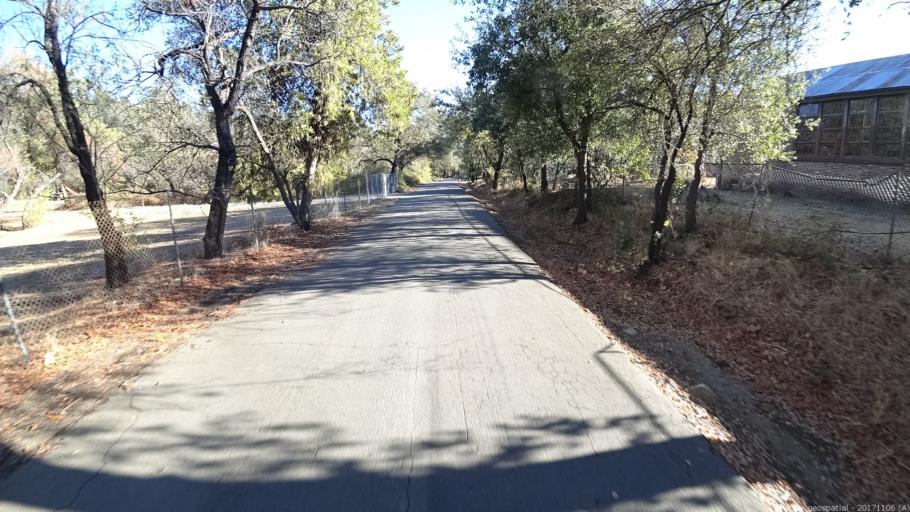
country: US
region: California
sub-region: Shasta County
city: Shasta
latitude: 40.5981
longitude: -122.4893
